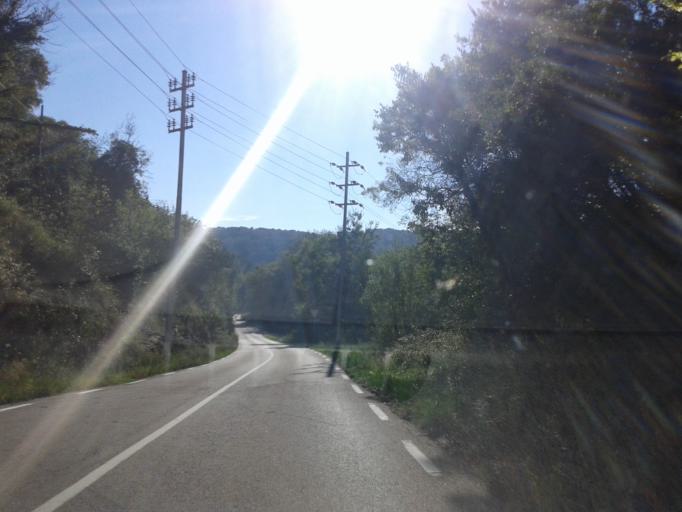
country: ES
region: Catalonia
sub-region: Provincia de Barcelona
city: Castellet
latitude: 41.2650
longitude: 1.6356
